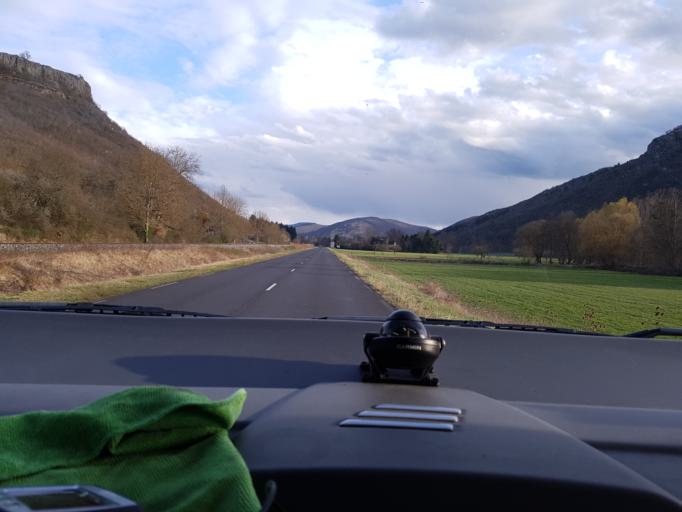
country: FR
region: Auvergne
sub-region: Departement du Cantal
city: Massiac
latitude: 45.2761
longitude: 3.1924
